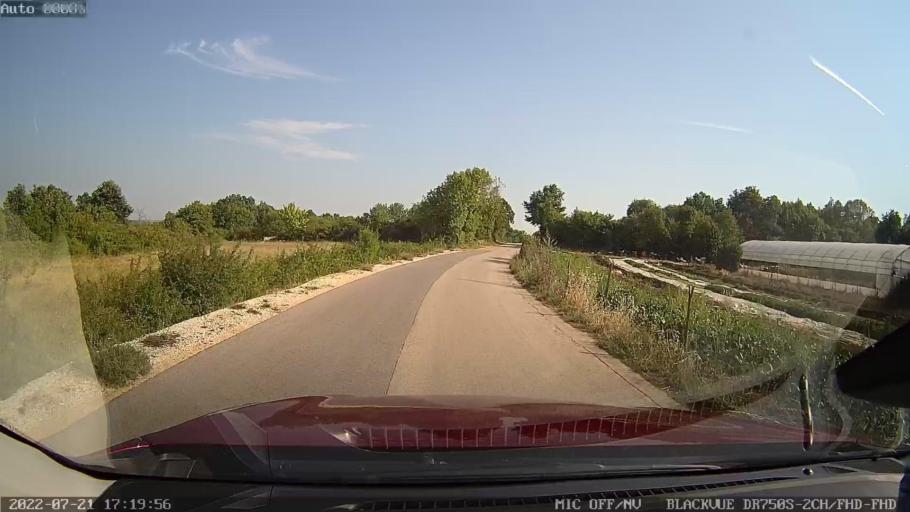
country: HR
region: Istarska
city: Karojba
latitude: 45.2082
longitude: 13.8277
